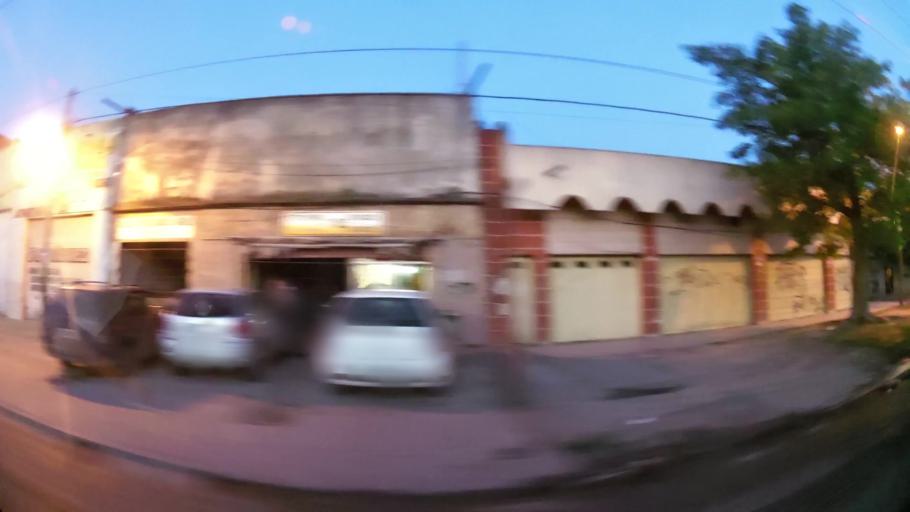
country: AR
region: Buenos Aires
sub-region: Partido de Almirante Brown
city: Adrogue
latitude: -34.7761
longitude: -58.3214
